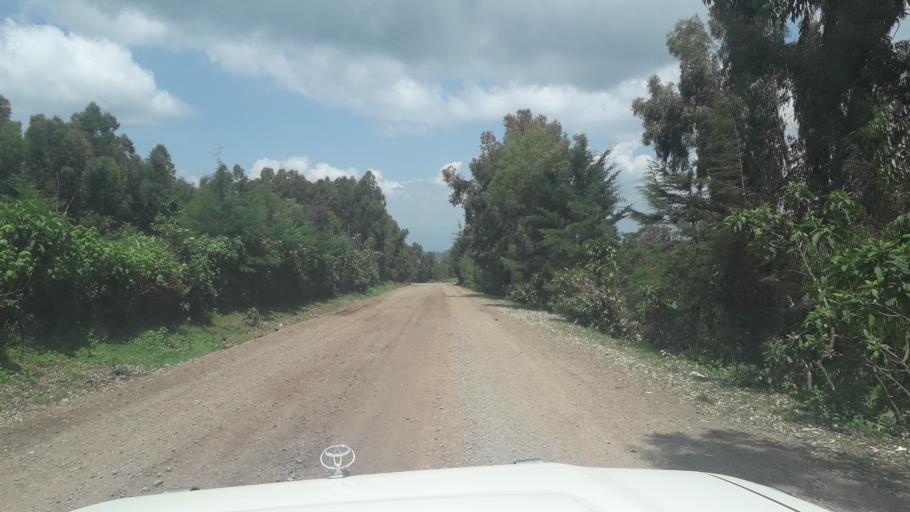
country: ET
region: Oromiya
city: Jima
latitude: 7.4544
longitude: 36.8708
